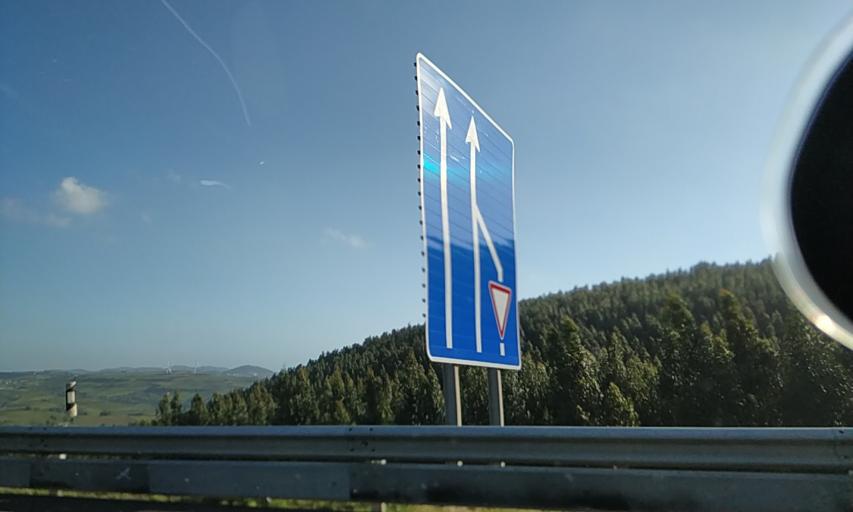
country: PT
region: Lisbon
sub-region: Sobral de Monte Agraco
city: Sobral de Monte Agraco
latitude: 39.0168
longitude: -9.2162
